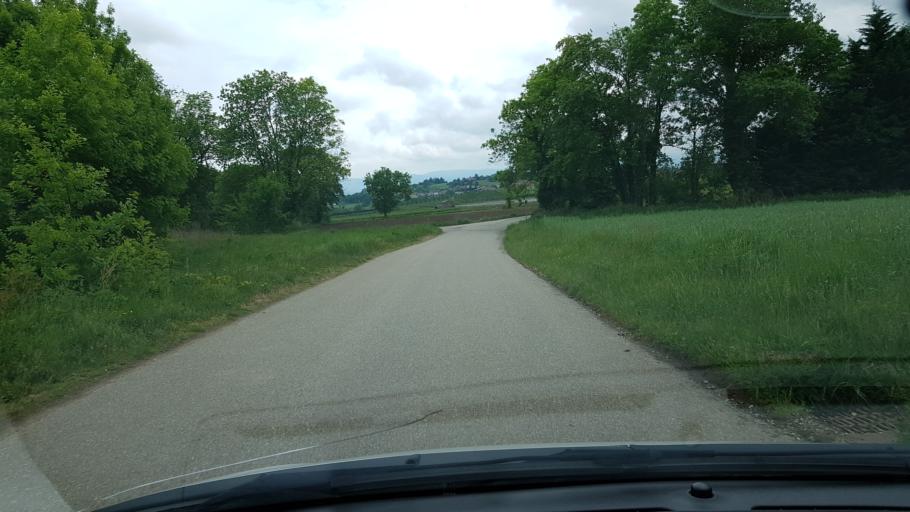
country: FR
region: Rhone-Alpes
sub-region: Departement du Rhone
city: Mornant
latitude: 45.6334
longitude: 4.6861
